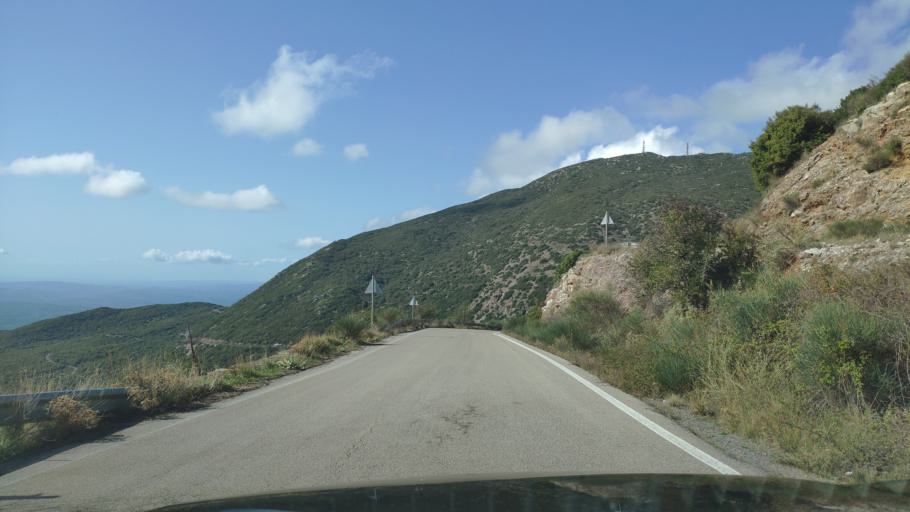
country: GR
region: Peloponnese
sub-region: Nomos Arkadias
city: Dimitsana
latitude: 37.5690
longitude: 22.0215
